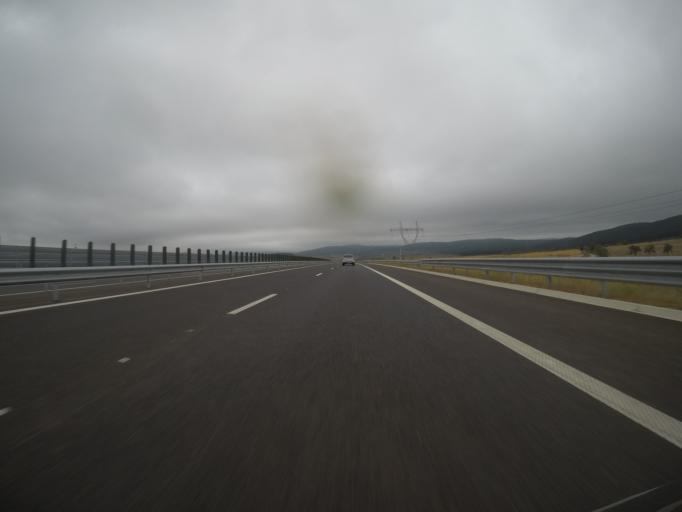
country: RO
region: Hunedoara
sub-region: Comuna Branisca
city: Branisca
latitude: 45.9188
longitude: 22.7827
